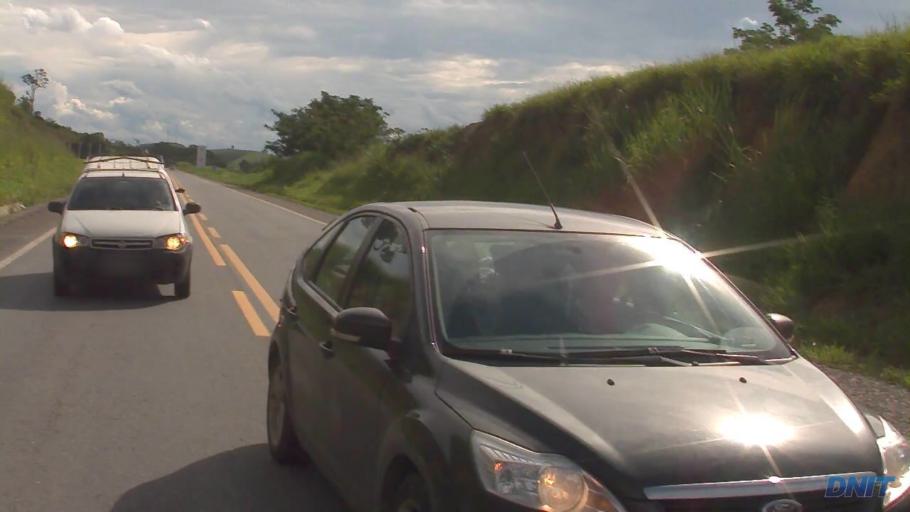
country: BR
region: Minas Gerais
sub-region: Belo Oriente
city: Belo Oriente
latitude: -19.2009
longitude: -42.2883
